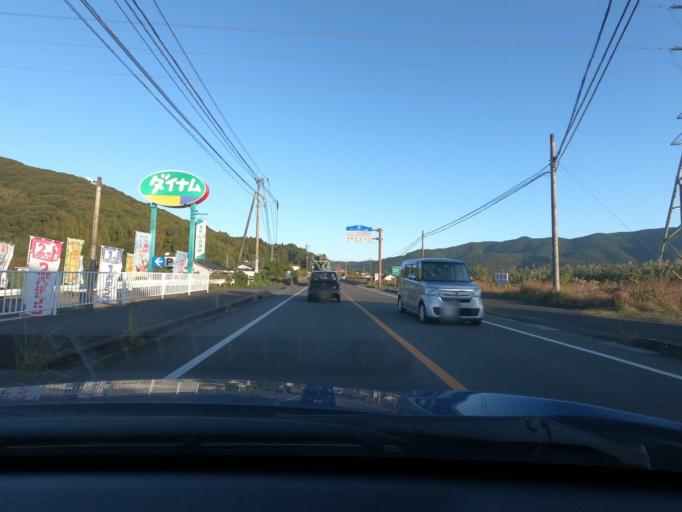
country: JP
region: Kagoshima
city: Satsumasendai
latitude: 31.8077
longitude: 130.3394
